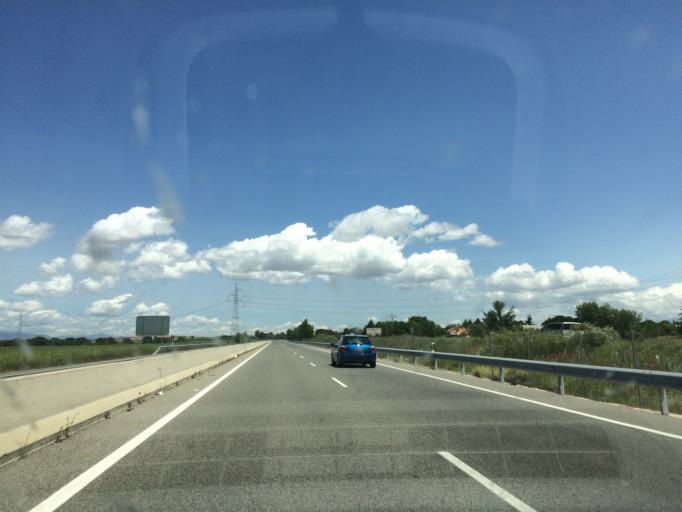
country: ES
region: Madrid
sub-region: Provincia de Madrid
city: Fuente el Saz
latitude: 40.6031
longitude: -3.5532
